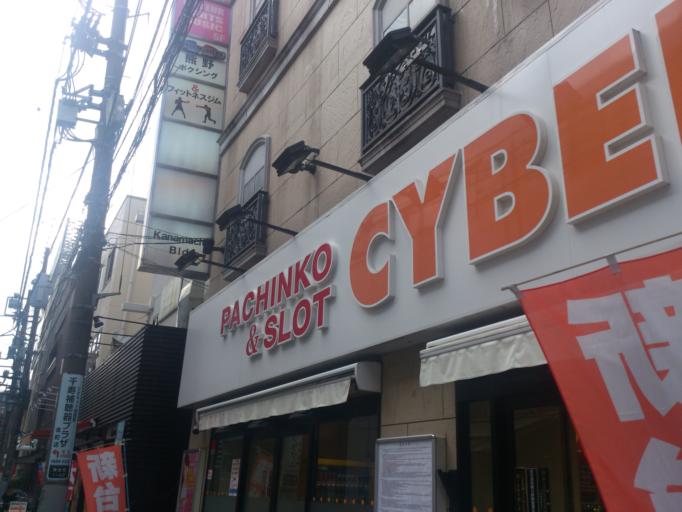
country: JP
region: Chiba
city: Matsudo
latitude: 35.7705
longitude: 139.8714
